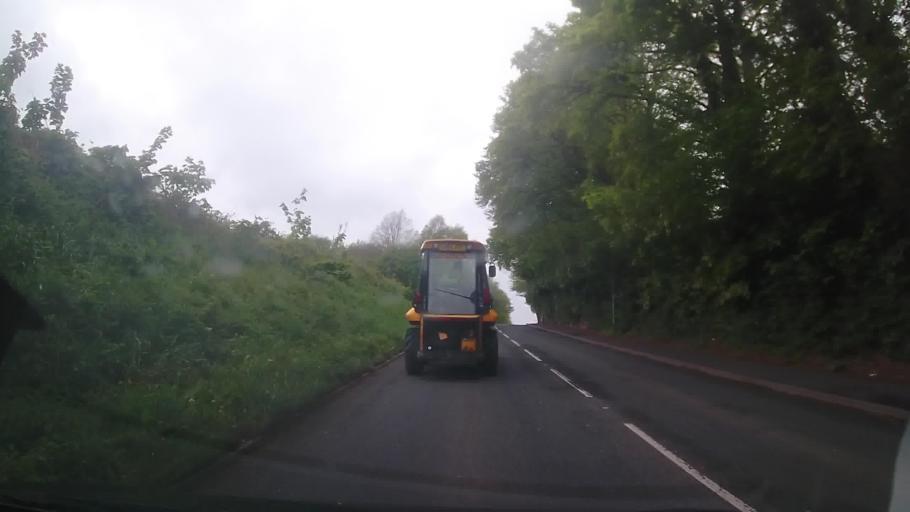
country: GB
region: Wales
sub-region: Wrexham
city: Ruabon
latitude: 52.9846
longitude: -3.0507
